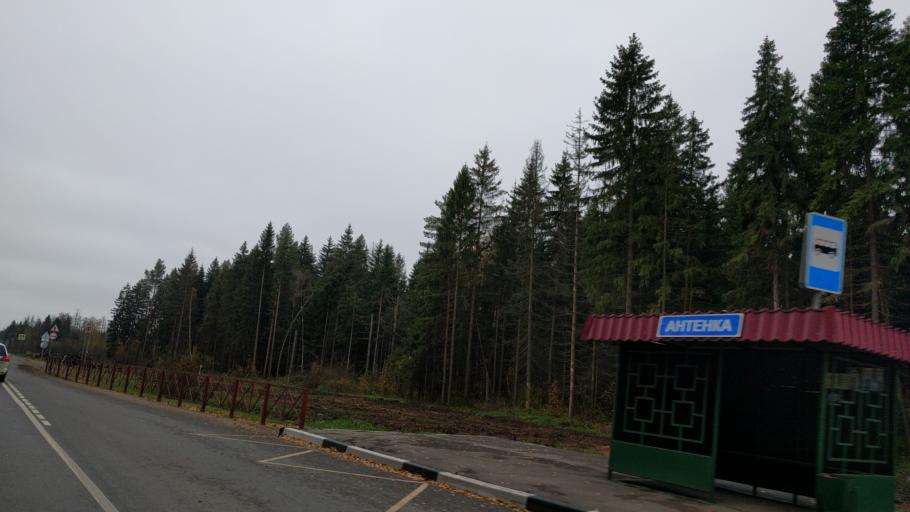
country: RU
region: Moskovskaya
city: Golitsyno
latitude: 55.5816
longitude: 37.0009
